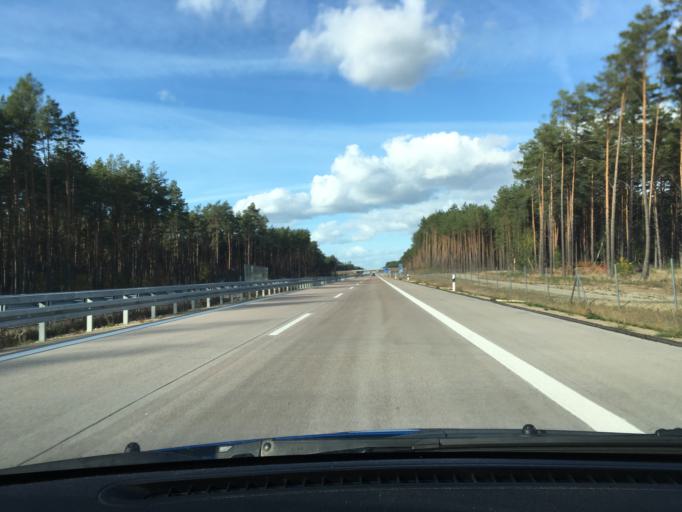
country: DE
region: Mecklenburg-Vorpommern
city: Grabow
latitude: 53.2909
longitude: 11.5271
